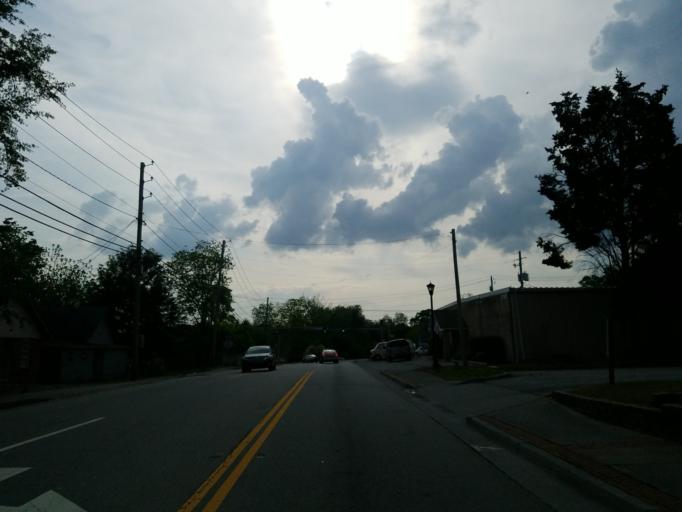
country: US
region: Georgia
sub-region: Cobb County
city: Austell
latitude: 33.8145
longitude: -84.6337
